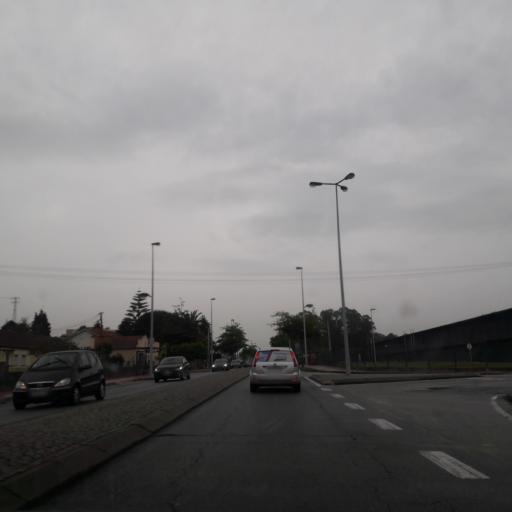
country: PT
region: Porto
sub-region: Vila do Conde
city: Arvore
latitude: 41.3279
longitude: -8.7175
